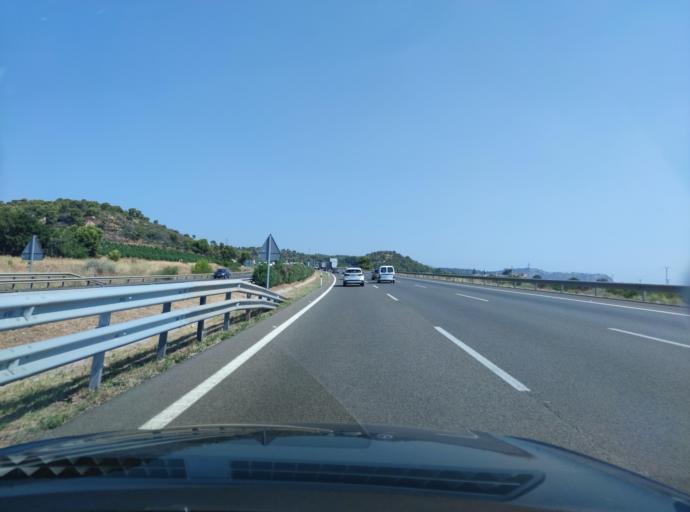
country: ES
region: Valencia
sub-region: Provincia de Valencia
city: Pucol
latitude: 39.6436
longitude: -0.3002
